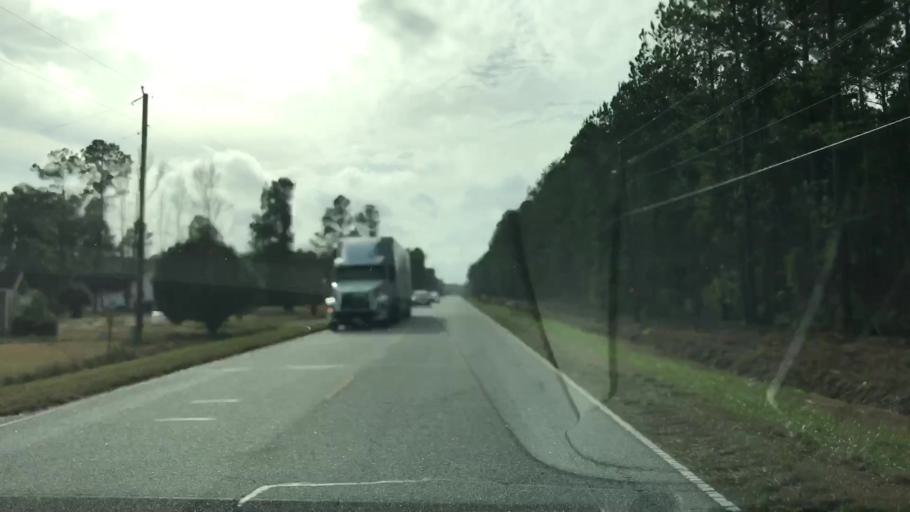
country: US
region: South Carolina
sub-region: Williamsburg County
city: Andrews
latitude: 33.3683
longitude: -79.6407
